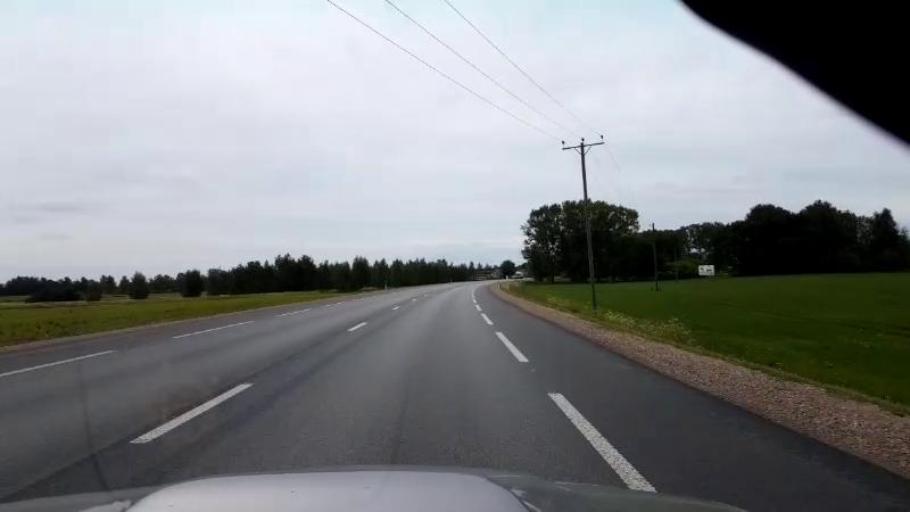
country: LV
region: Lecava
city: Iecava
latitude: 56.6082
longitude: 24.2119
